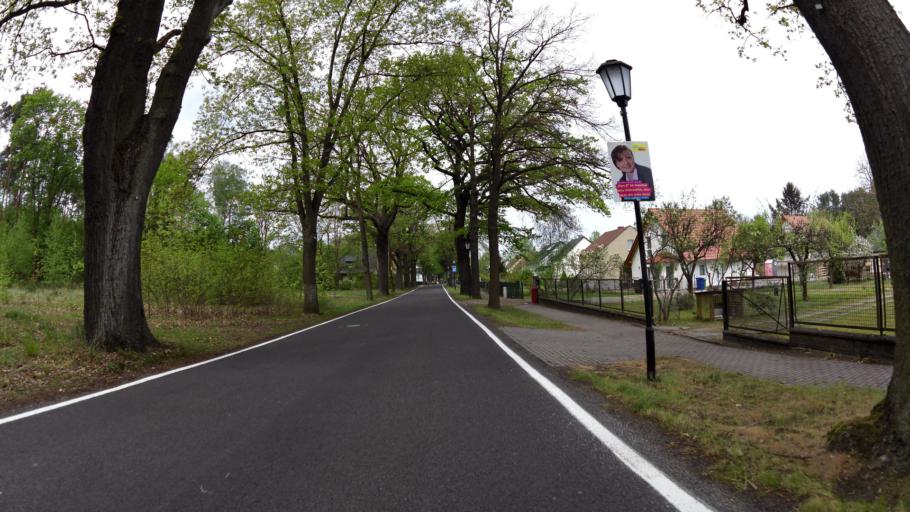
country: DE
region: Brandenburg
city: Mittenwalde
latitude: 52.2077
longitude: 13.5643
